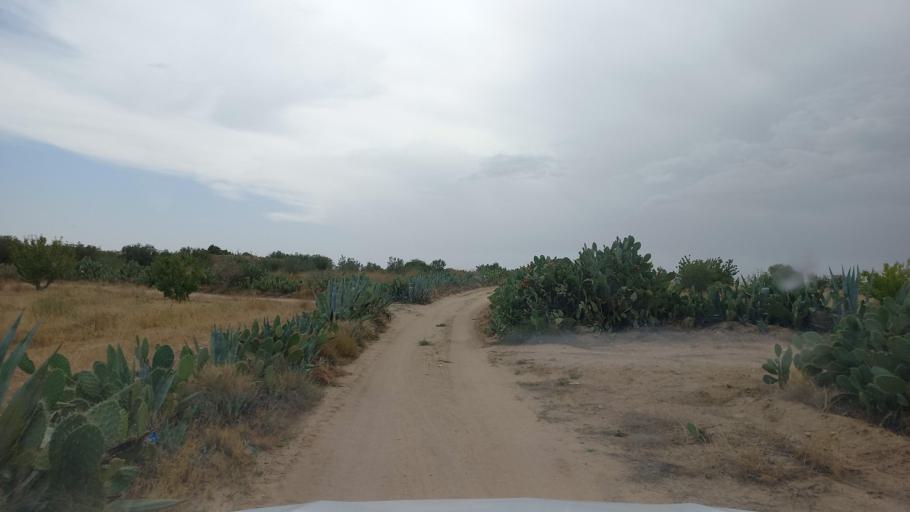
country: TN
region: Al Qasrayn
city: Kasserine
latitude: 35.2384
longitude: 9.0177
